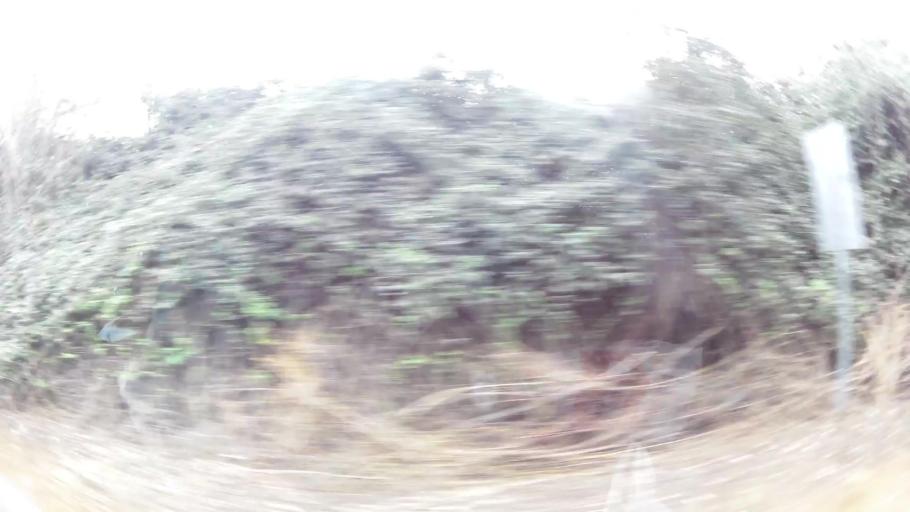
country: CL
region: Santiago Metropolitan
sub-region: Provincia de Chacabuco
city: Chicureo Abajo
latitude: -33.2669
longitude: -70.7161
